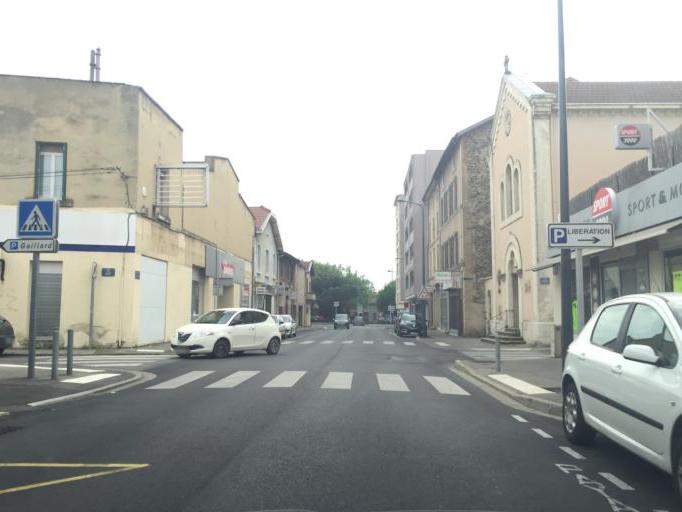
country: FR
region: Rhone-Alpes
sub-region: Departement de la Drome
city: Romans-sur-Isere
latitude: 45.0465
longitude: 5.0467
